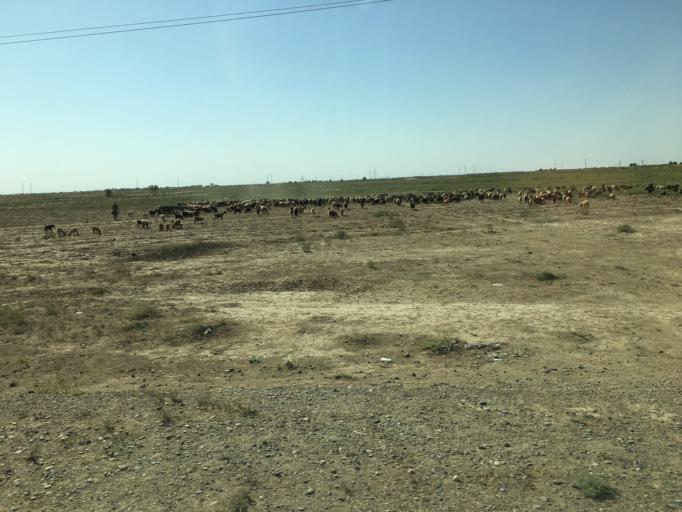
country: IR
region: Razavi Khorasan
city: Sarakhs
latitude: 36.5038
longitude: 61.2535
